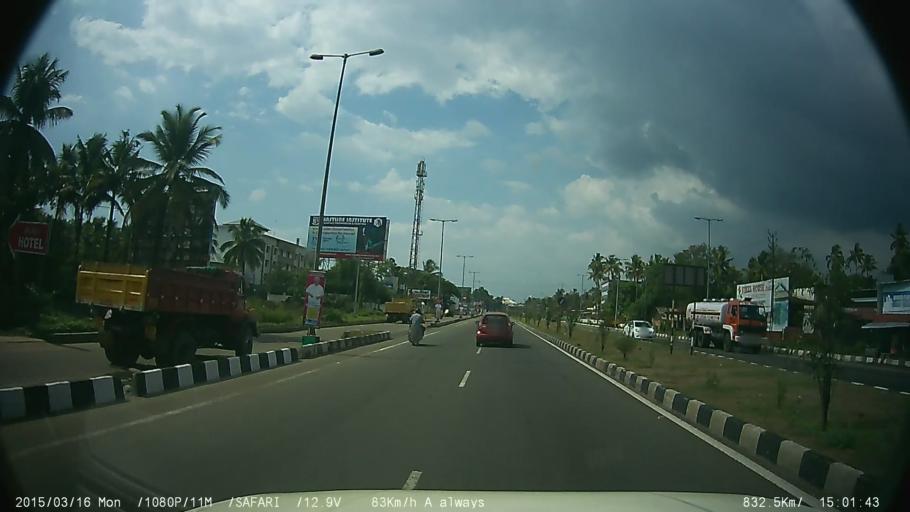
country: IN
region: Kerala
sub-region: Ernakulam
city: Angamali
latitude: 10.2270
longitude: 76.3748
